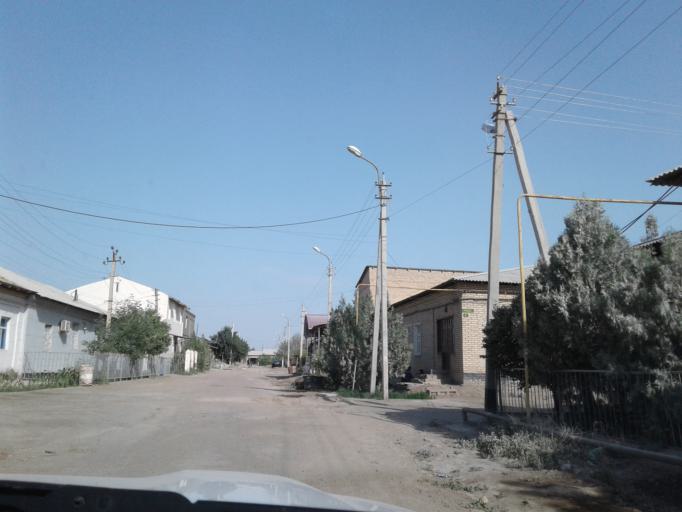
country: TM
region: Dasoguz
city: Dasoguz
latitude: 41.8486
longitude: 59.9241
